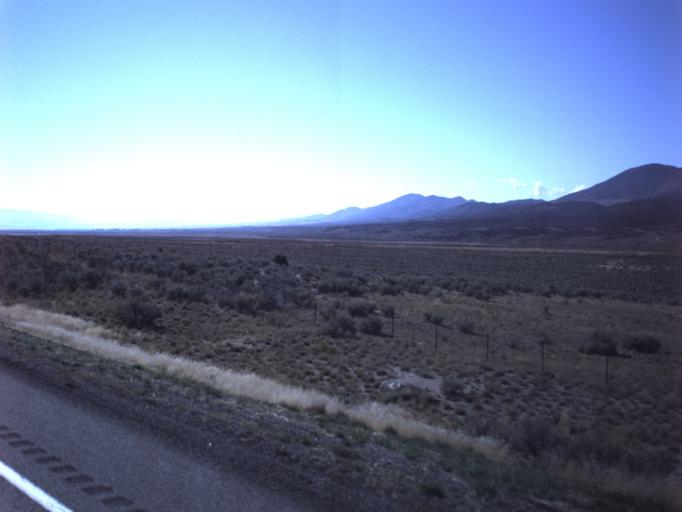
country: US
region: Utah
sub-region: Sanpete County
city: Gunnison
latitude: 39.3245
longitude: -111.9101
